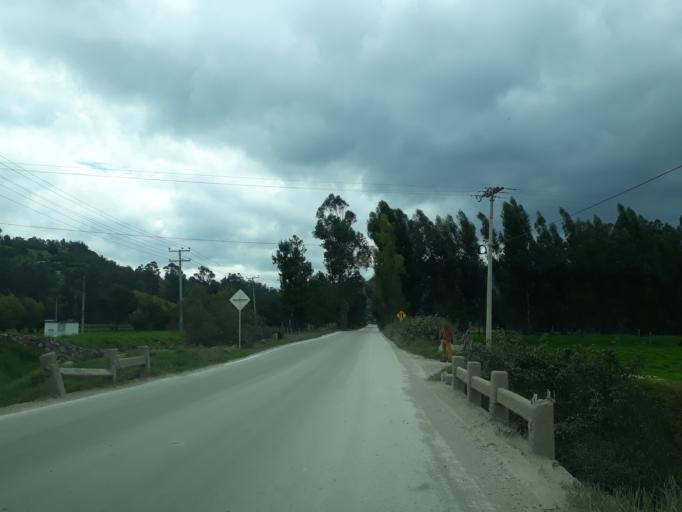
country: CO
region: Cundinamarca
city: Ubate
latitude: 5.3240
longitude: -73.7689
